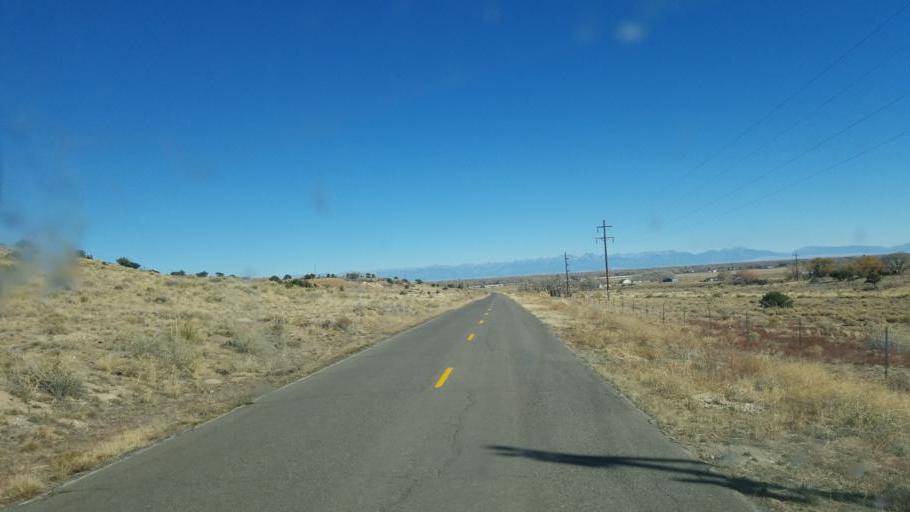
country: US
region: Colorado
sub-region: Rio Grande County
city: Del Norte
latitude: 37.6649
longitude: -106.3526
